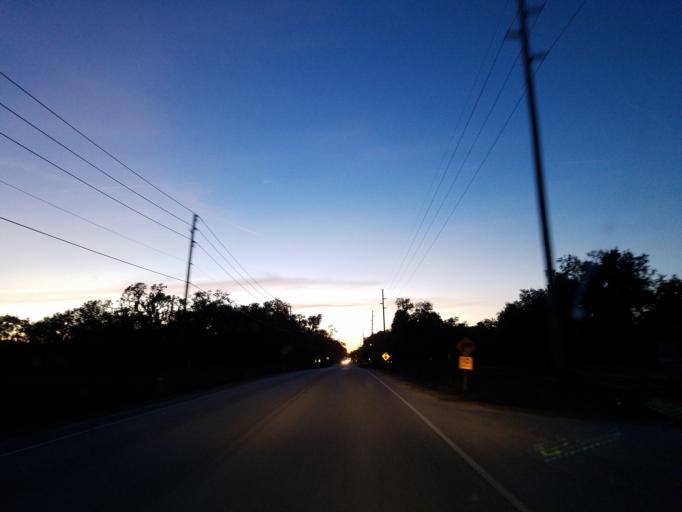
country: US
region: Florida
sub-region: Sumter County
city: Lake Panasoffkee
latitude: 28.7998
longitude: -82.0463
